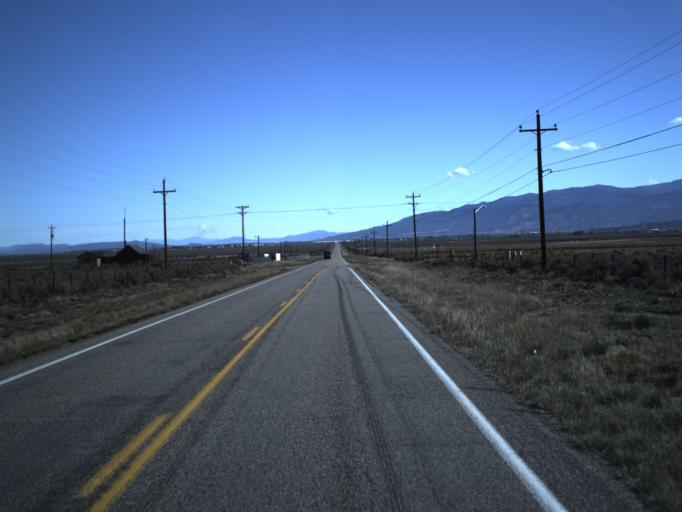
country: US
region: Utah
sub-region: Iron County
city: Cedar City
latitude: 37.6579
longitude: -113.2179
